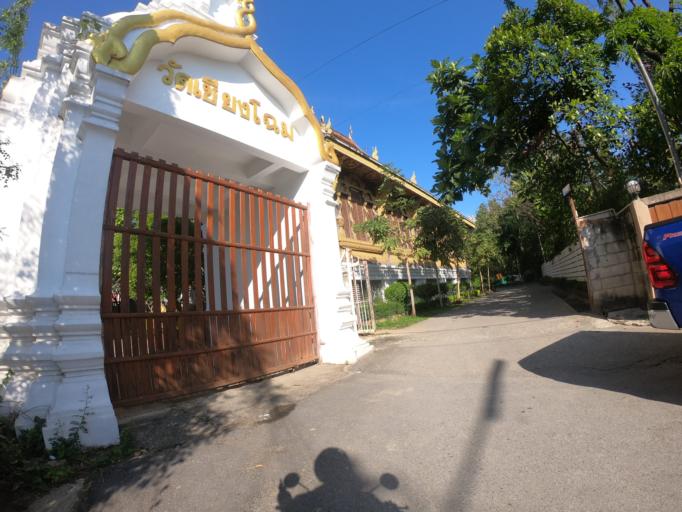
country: TH
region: Chiang Mai
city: Chiang Mai
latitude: 18.8071
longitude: 98.9823
